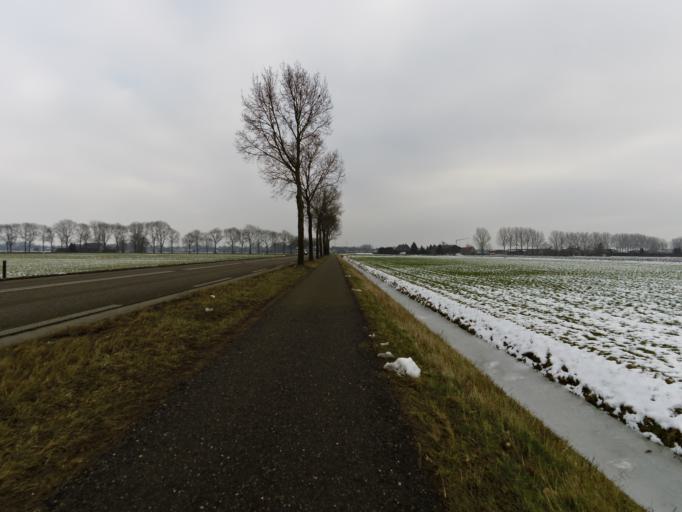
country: NL
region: Gelderland
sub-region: Gemeente Zevenaar
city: Zevenaar
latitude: 51.9428
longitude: 6.0448
